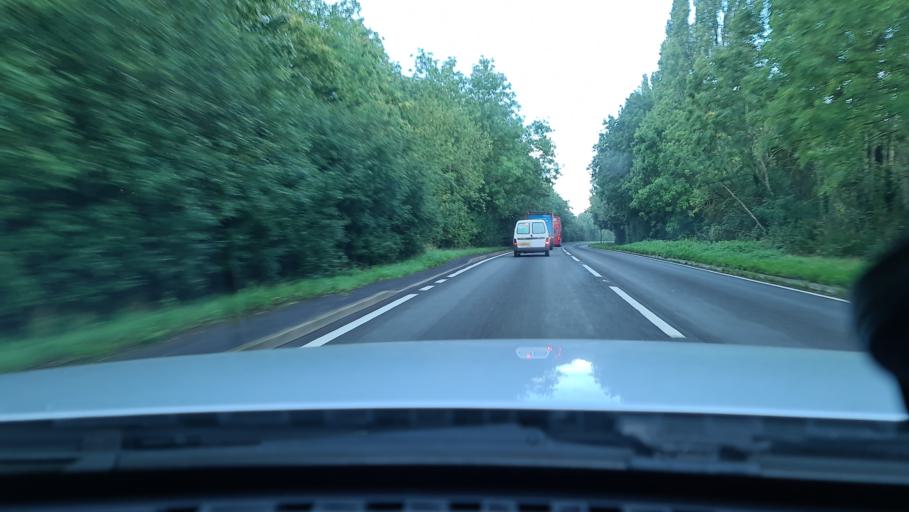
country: GB
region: England
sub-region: Warwickshire
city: Long Itchington
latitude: 52.2696
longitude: -1.3895
